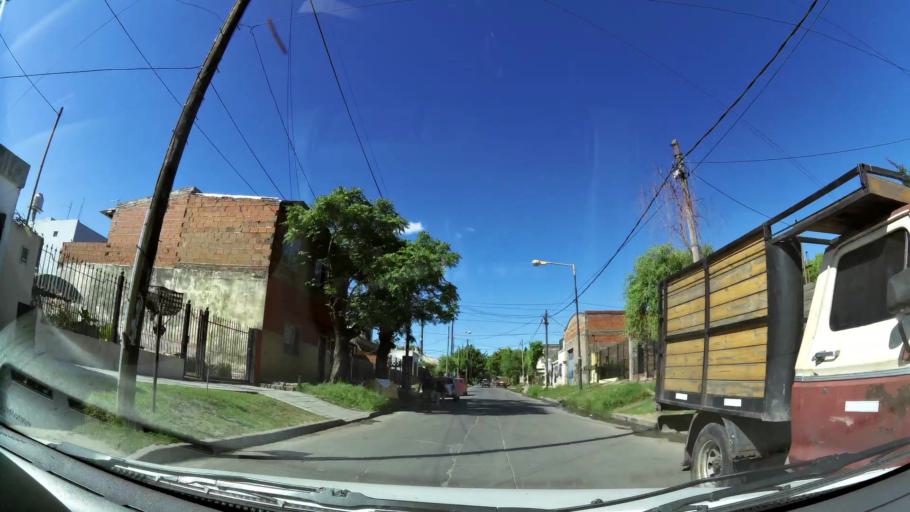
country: AR
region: Buenos Aires
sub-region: Partido de Tigre
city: Tigre
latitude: -34.5100
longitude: -58.5826
